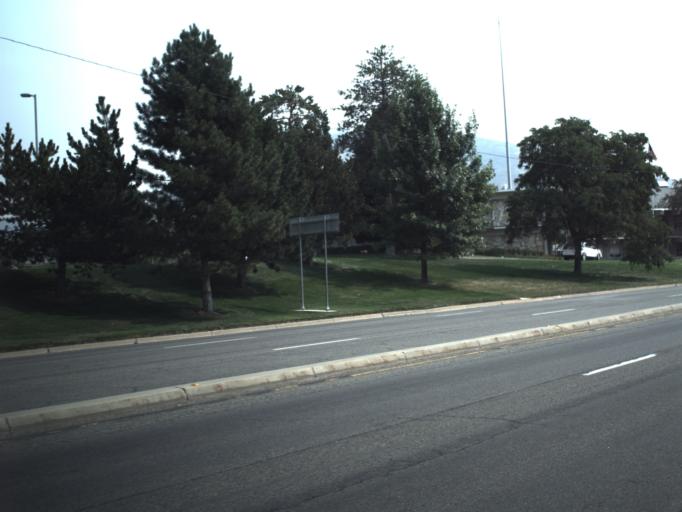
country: US
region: Utah
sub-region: Salt Lake County
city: Willard
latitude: 40.7583
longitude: -111.8388
